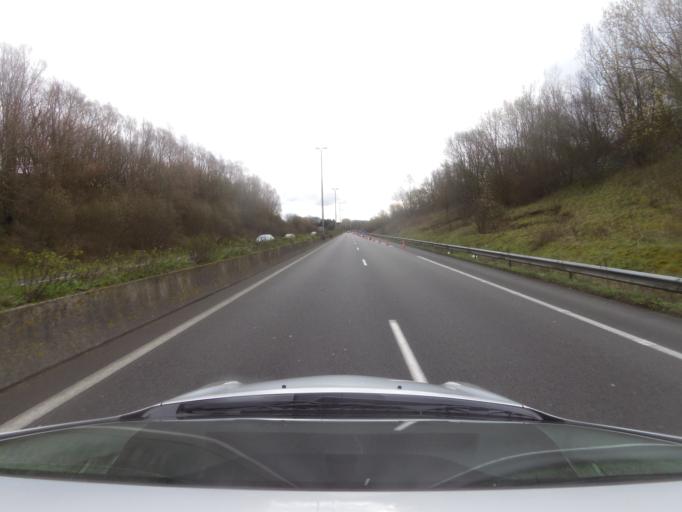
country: FR
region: Nord-Pas-de-Calais
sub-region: Departement du Pas-de-Calais
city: Saint-Martin-Boulogne
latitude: 50.7353
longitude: 1.6392
